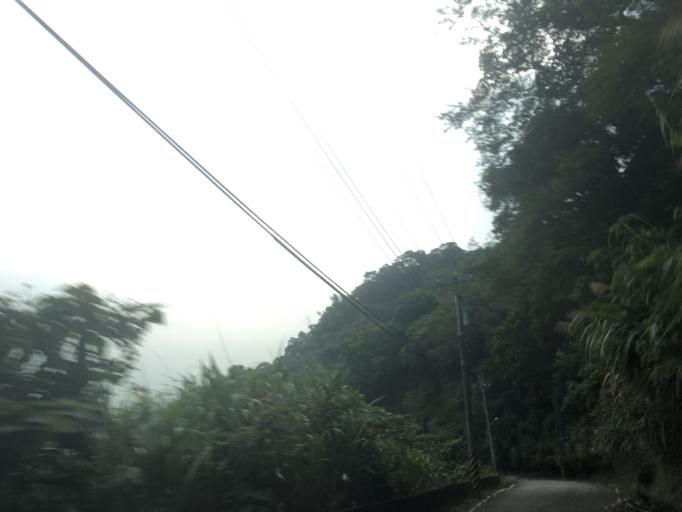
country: TW
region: Taiwan
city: Fengyuan
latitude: 24.1873
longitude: 120.7815
